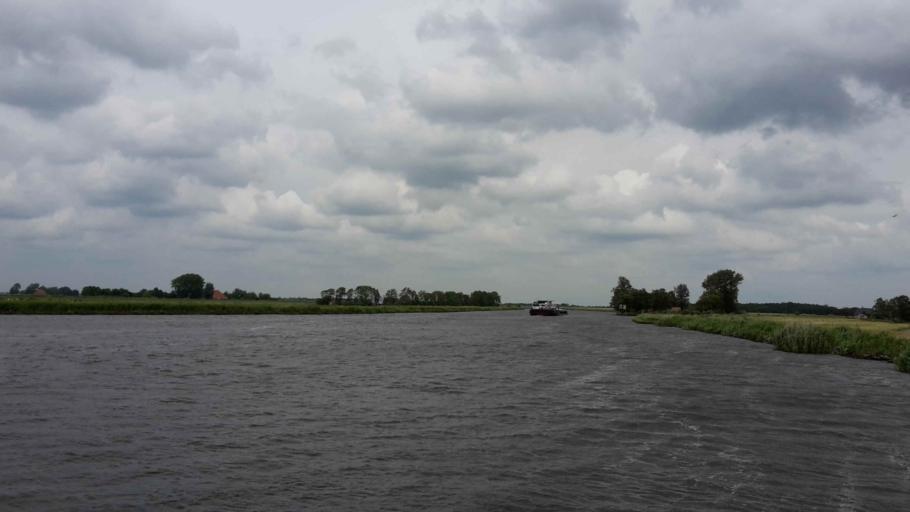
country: NL
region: Friesland
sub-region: Gemeente Boarnsterhim
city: Grou
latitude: 53.1091
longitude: 5.8622
